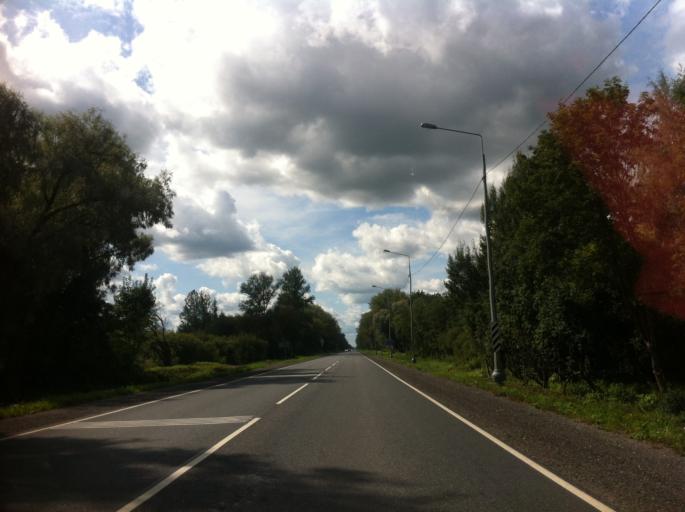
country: RU
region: Pskov
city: Pskov
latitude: 57.7791
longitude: 28.1598
